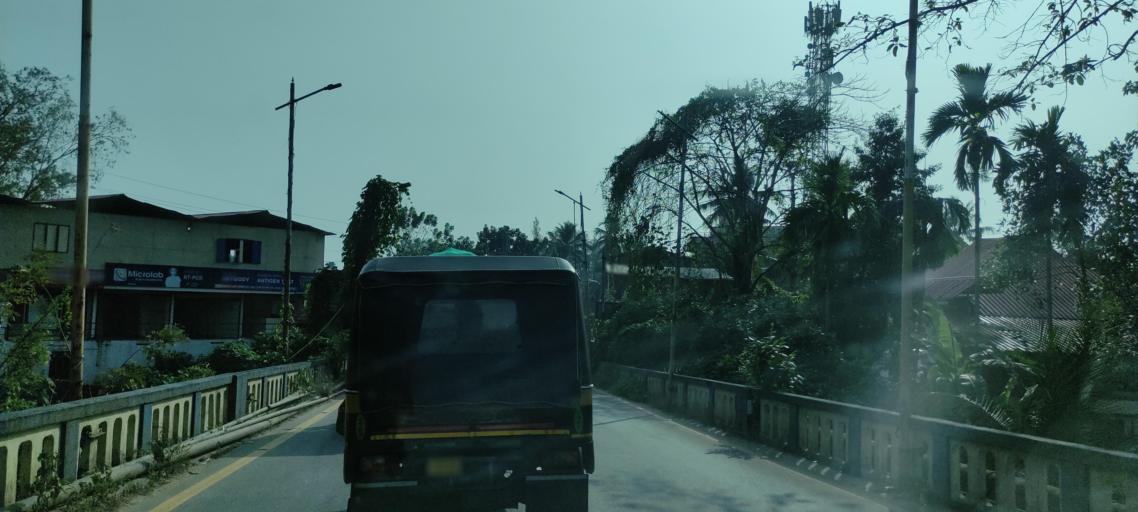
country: IN
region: Kerala
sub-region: Kottayam
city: Changanacheri
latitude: 9.3638
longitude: 76.4764
